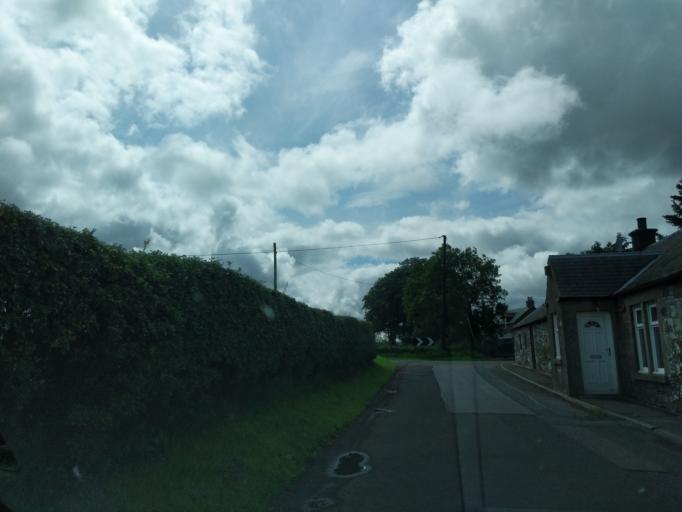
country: GB
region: Scotland
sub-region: South Lanarkshire
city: Lanark
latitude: 55.6210
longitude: -3.6995
